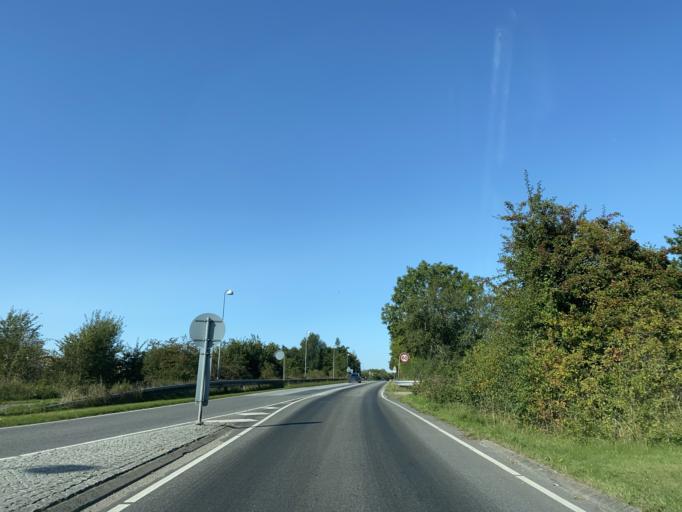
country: DK
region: South Denmark
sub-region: Aabenraa Kommune
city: Aabenraa
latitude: 55.0611
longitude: 9.3861
